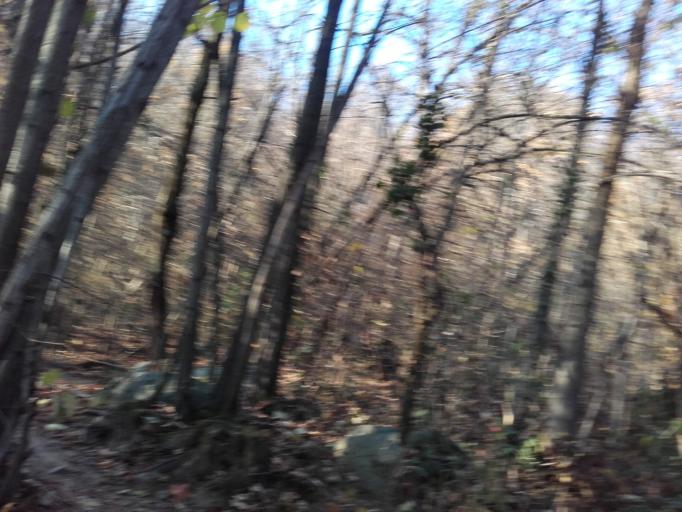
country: IT
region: Piedmont
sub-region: Provincia di Torino
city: San Mauro Torinese
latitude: 45.0750
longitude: 7.7686
